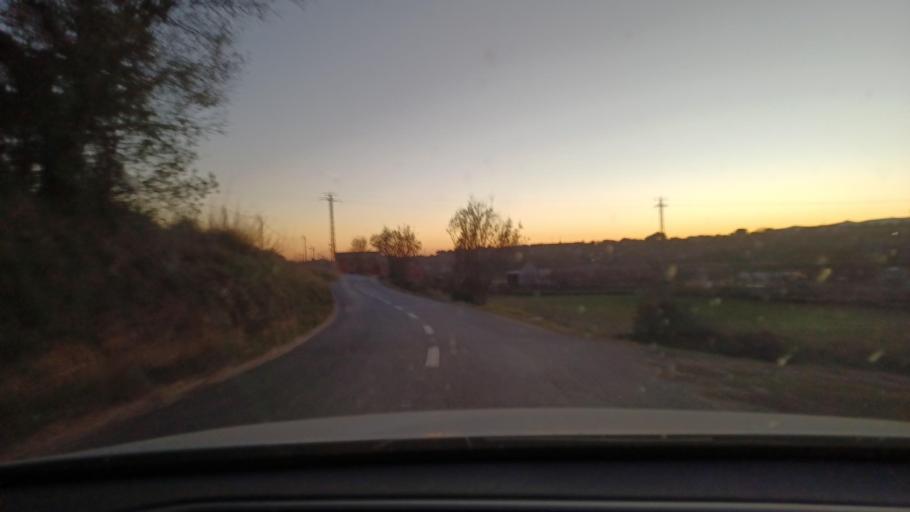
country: ES
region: Catalonia
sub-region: Provincia de Barcelona
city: Vilafranca del Penedes
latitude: 41.3588
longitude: 1.6725
